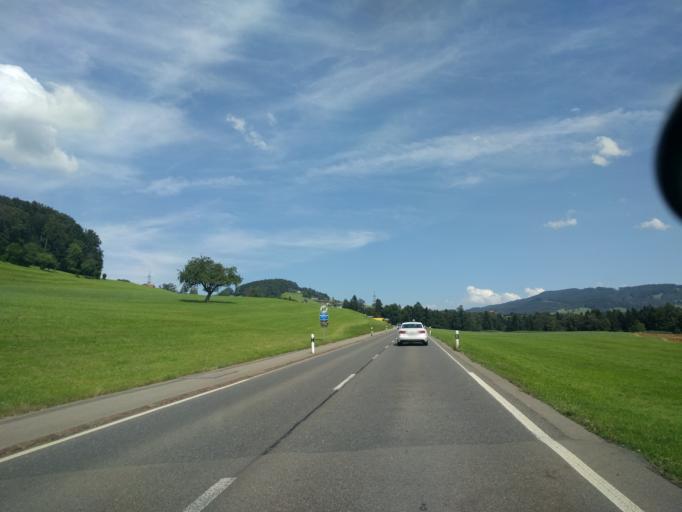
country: CH
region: Saint Gallen
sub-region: Wahlkreis See-Gaster
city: Sankt Gallenkappel
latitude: 47.2498
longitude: 8.9860
